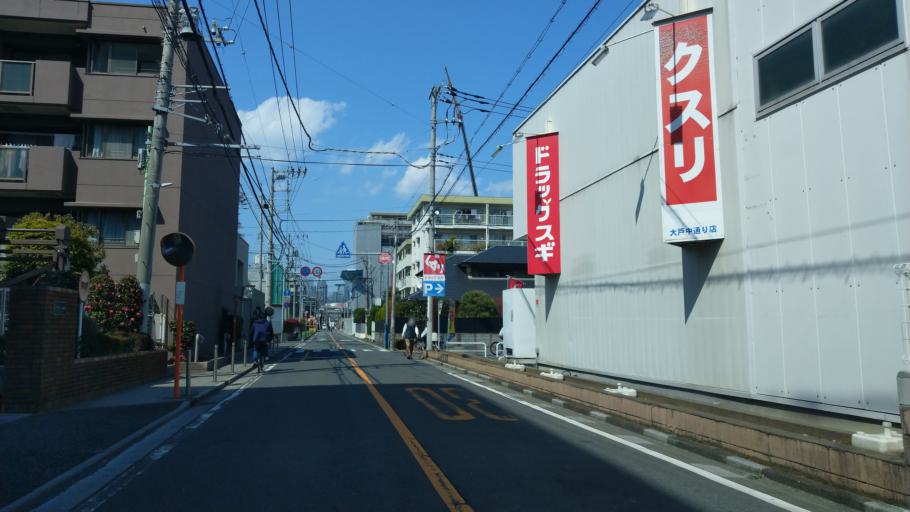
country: JP
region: Saitama
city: Yono
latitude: 35.8710
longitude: 139.6368
